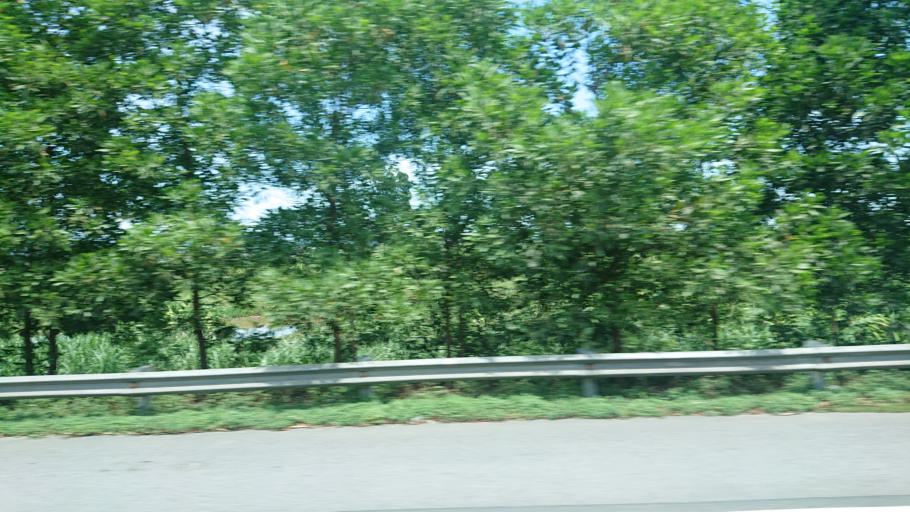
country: VN
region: Ha Nam
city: Thanh Pho Phu Ly
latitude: 20.5623
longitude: 105.9497
